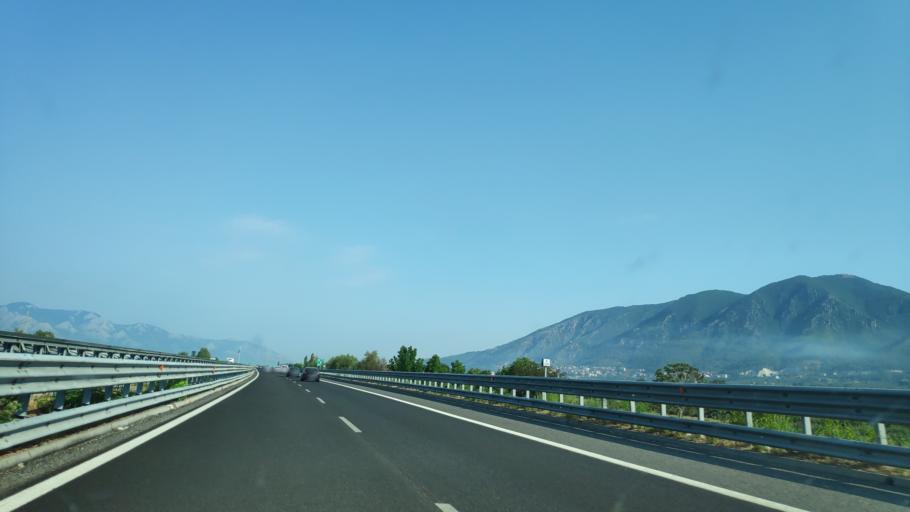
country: IT
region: Campania
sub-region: Provincia di Salerno
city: Sala Consilina
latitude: 40.3615
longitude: 15.6089
